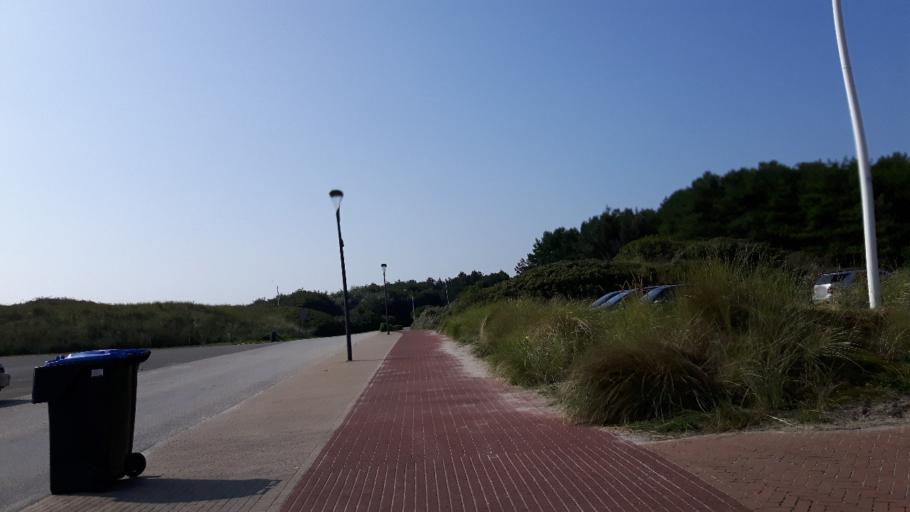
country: NL
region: Friesland
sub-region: Gemeente Ameland
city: Nes
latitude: 53.4598
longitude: 5.8076
